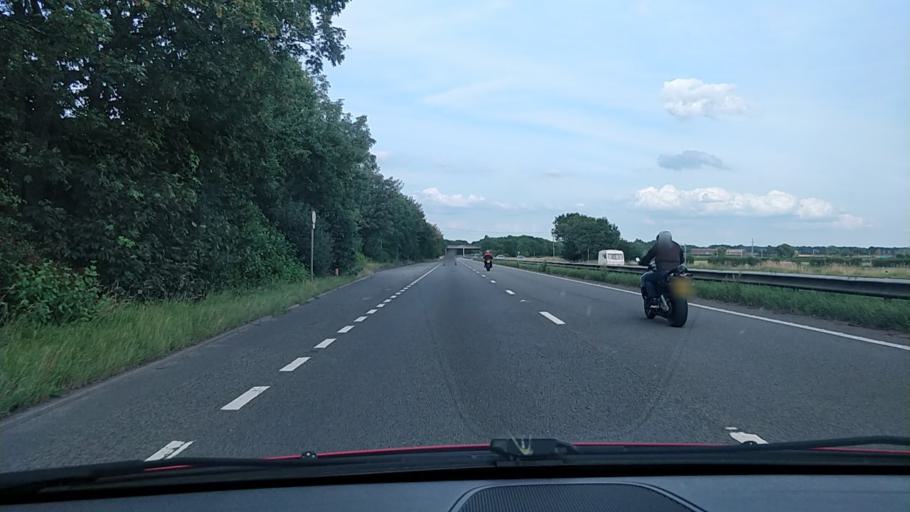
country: GB
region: Wales
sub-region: County of Flintshire
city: Hawarden
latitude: 53.1619
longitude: -2.9834
